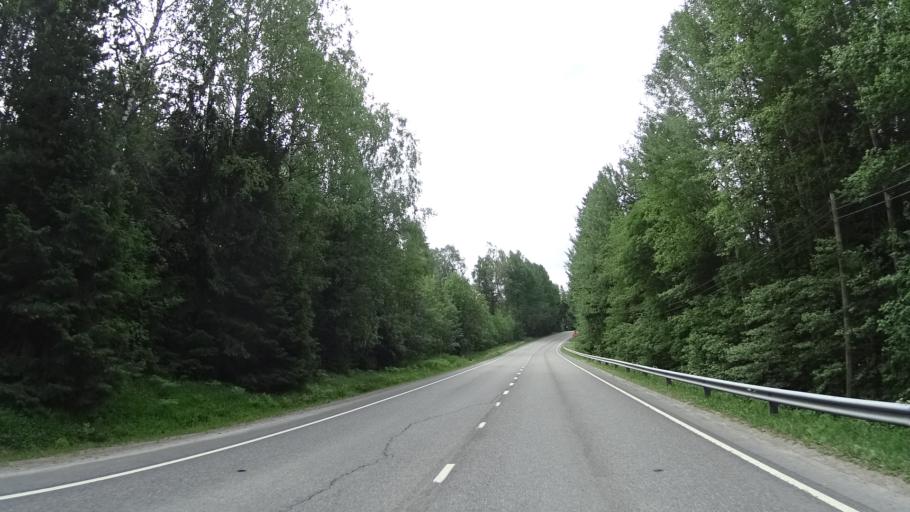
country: FI
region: Uusimaa
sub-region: Helsinki
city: Vihti
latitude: 60.2854
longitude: 24.4074
